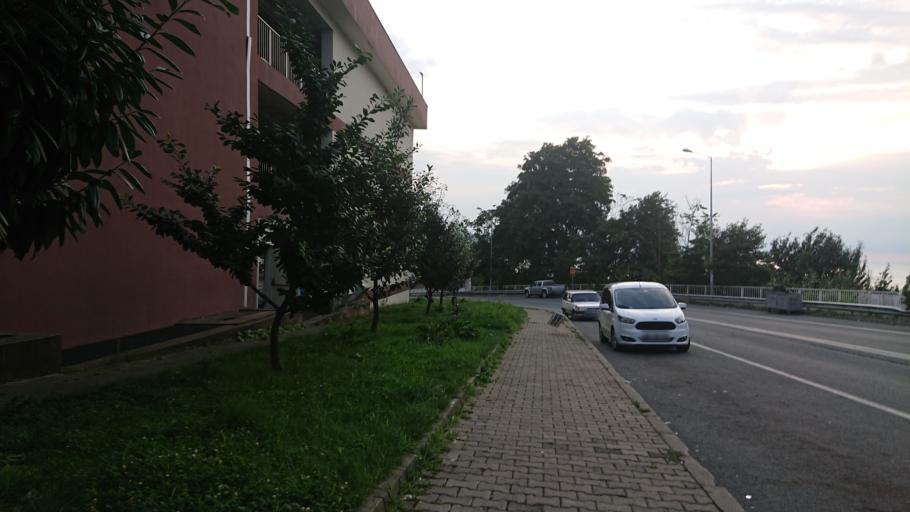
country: TR
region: Rize
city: Gundogdu
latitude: 41.0392
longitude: 40.5726
